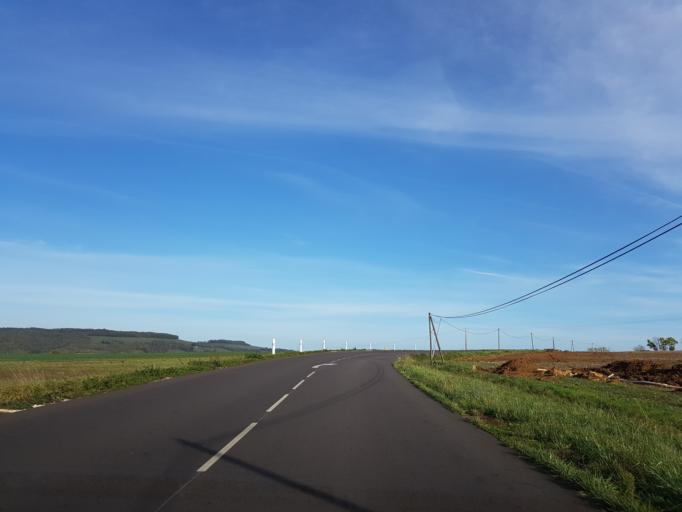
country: FR
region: Bourgogne
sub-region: Departement de la Cote-d'Or
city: Semur-en-Auxois
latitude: 47.4948
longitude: 4.3135
